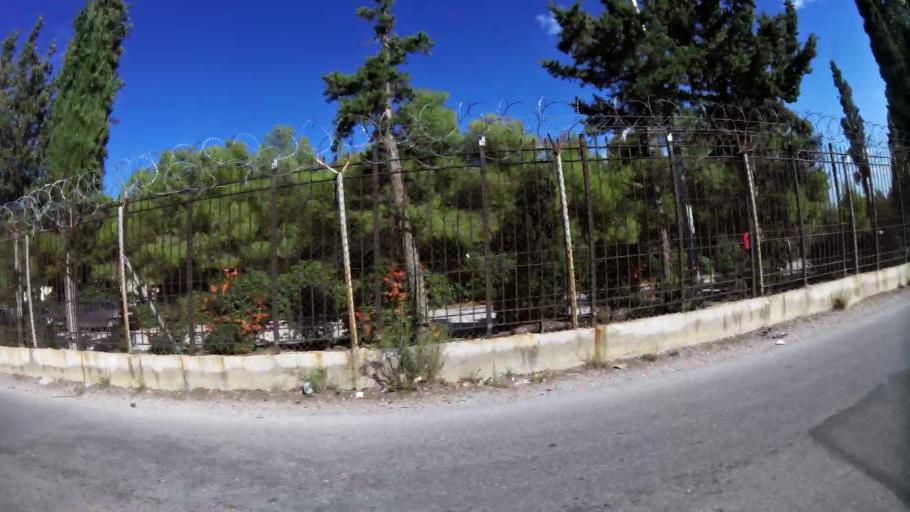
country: GR
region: Attica
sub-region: Nomarchia Anatolikis Attikis
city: Acharnes
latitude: 38.1038
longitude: 23.7237
